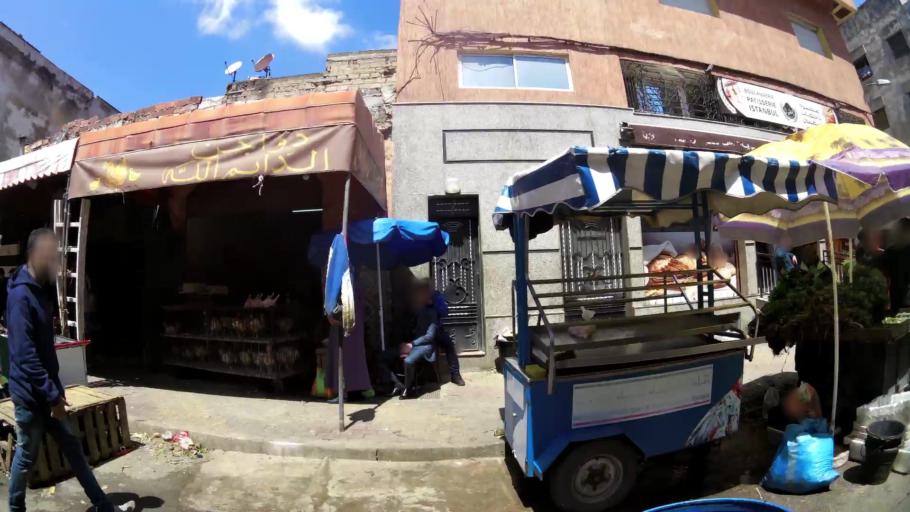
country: MA
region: Grand Casablanca
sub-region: Casablanca
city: Casablanca
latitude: 33.5696
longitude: -7.5980
